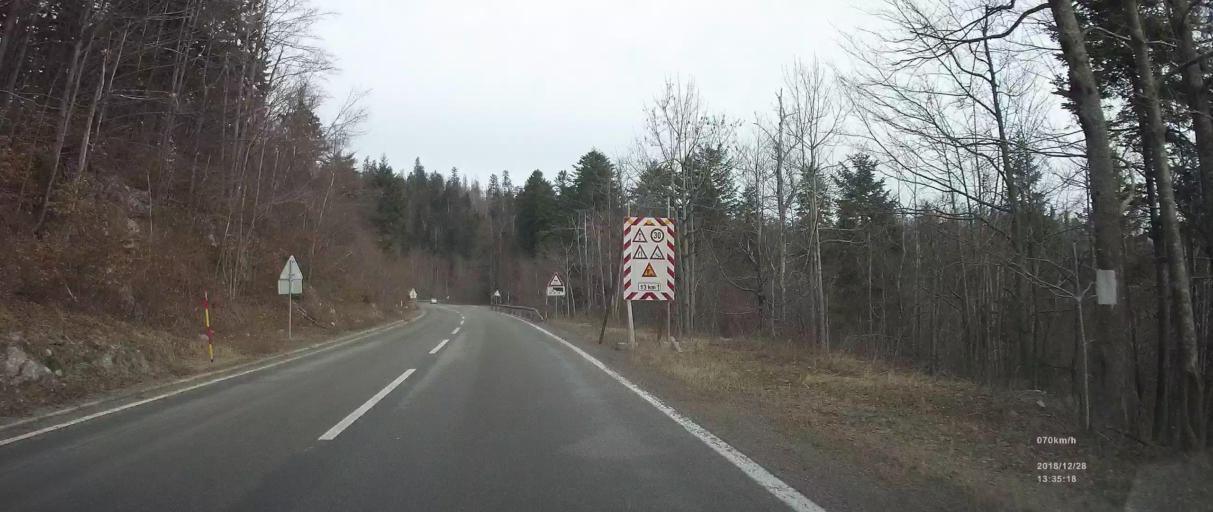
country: HR
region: Primorsko-Goranska
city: Hreljin
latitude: 45.3485
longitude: 14.6911
